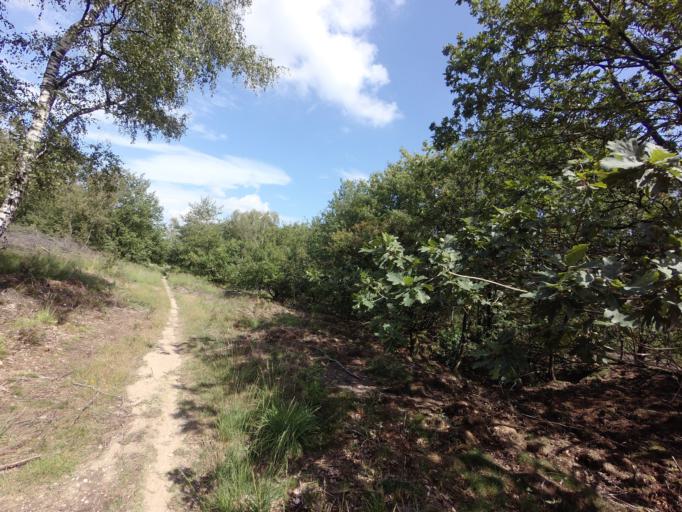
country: NL
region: Gelderland
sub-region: Gemeente Ede
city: Ede
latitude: 52.0517
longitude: 5.6978
